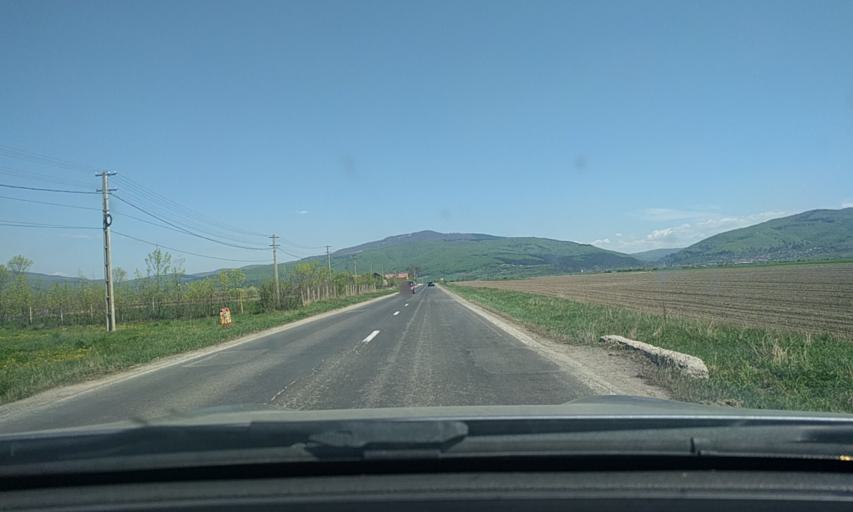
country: RO
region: Brasov
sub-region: Comuna Prejmer
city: Prejmer
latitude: 45.7132
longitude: 25.8024
